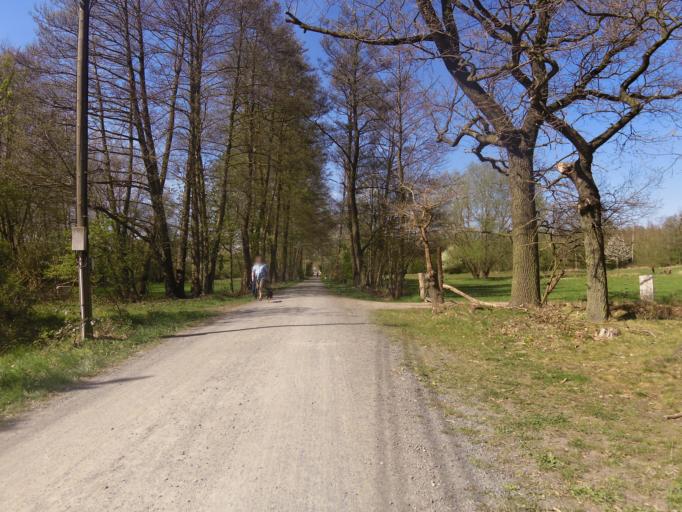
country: DE
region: Hesse
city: Morfelden-Walldorf
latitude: 49.9760
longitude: 8.5966
